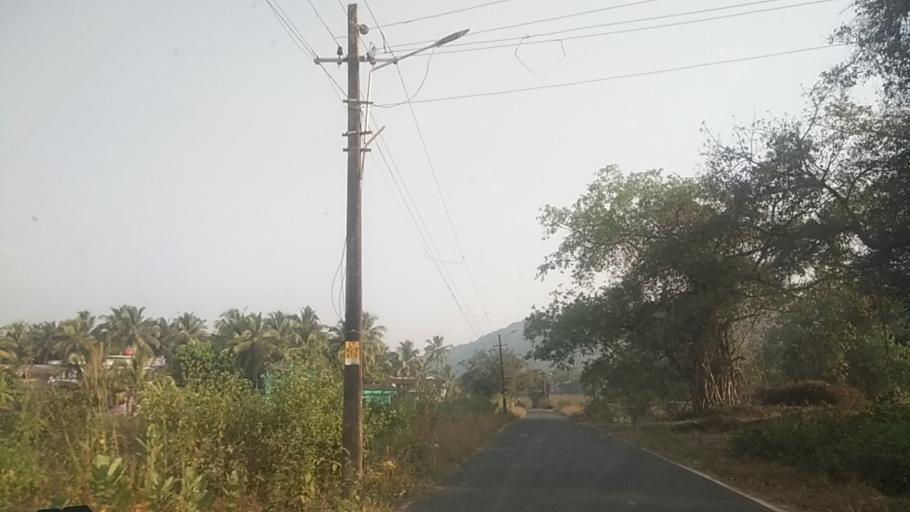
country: IN
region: Goa
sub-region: South Goa
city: Chinchinim
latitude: 15.2281
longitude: 73.9917
